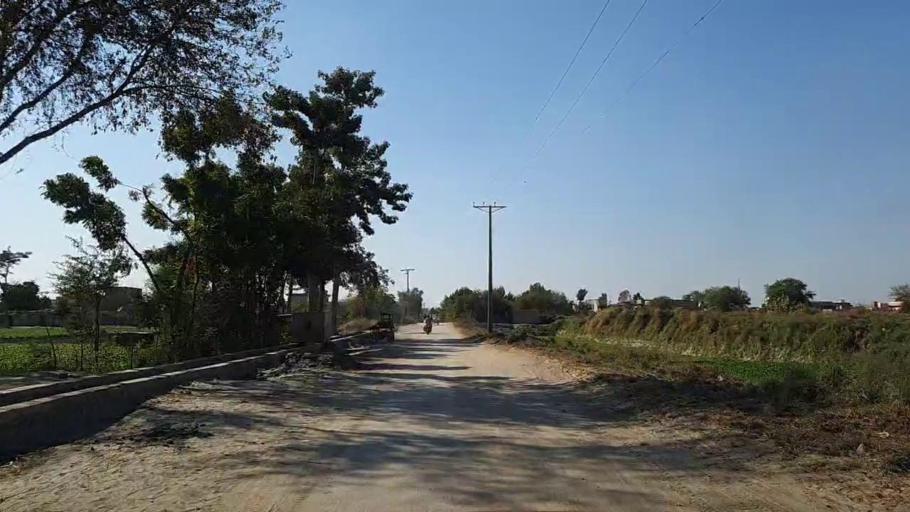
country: PK
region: Sindh
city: Nawabshah
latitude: 26.2442
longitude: 68.4289
